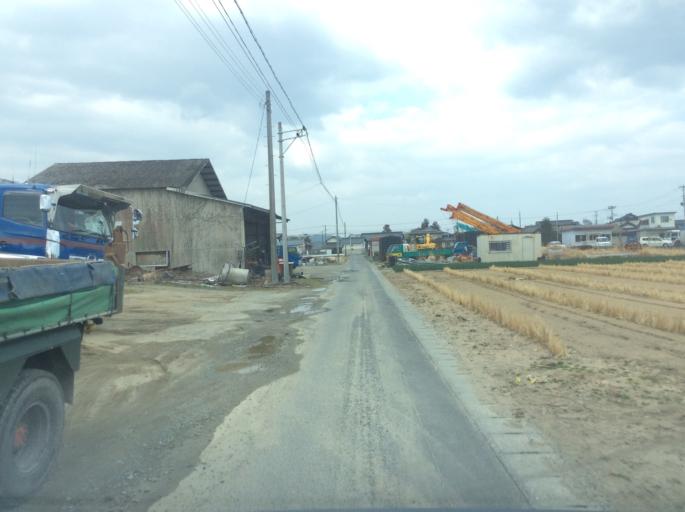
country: JP
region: Fukushima
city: Iwaki
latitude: 37.0795
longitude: 140.9723
